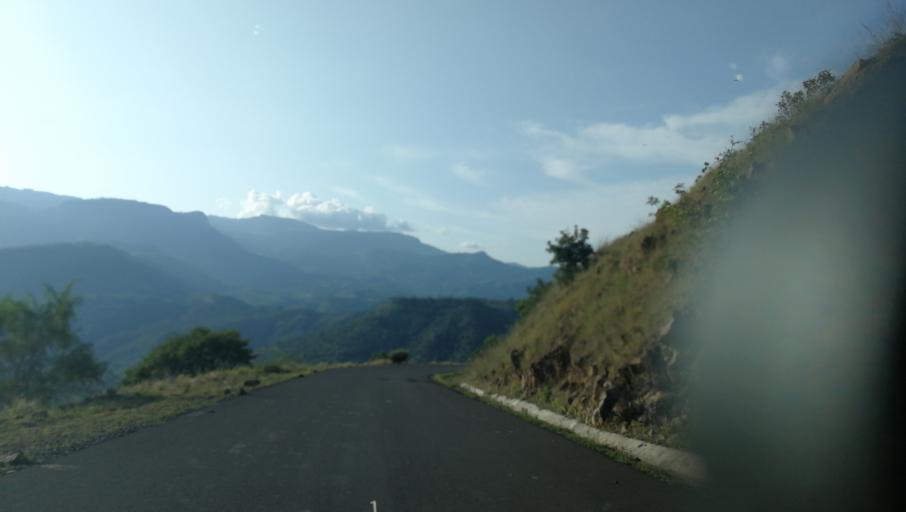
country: ET
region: Southern Nations, Nationalities, and People's Region
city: Areka
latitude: 6.8273
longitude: 37.3023
